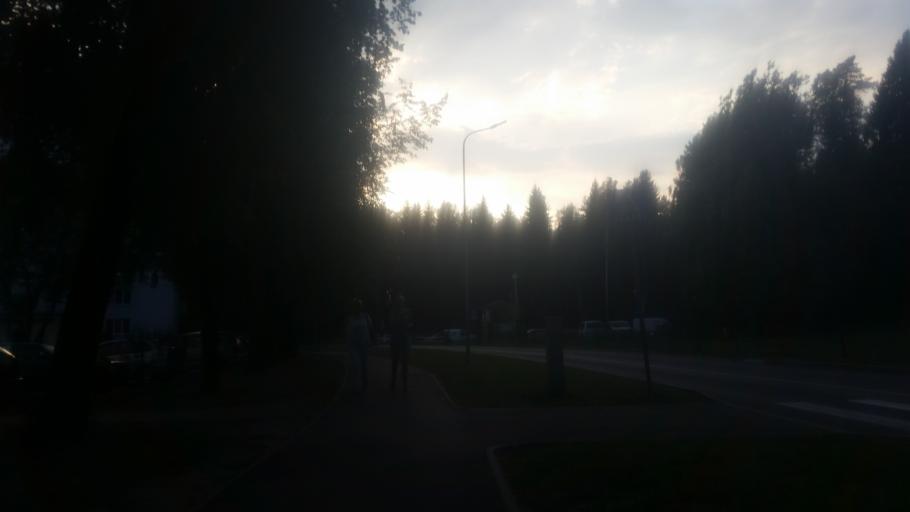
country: LV
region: Ogre
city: Ogre
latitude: 56.8259
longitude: 24.5946
